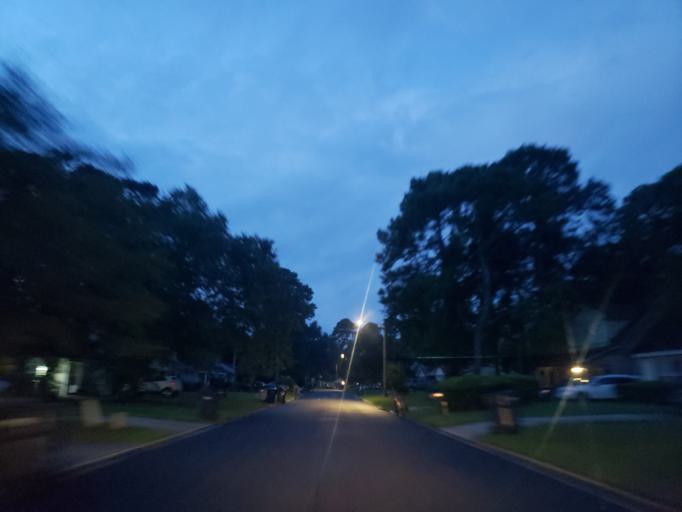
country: US
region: Georgia
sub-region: Chatham County
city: Isle of Hope
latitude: 31.9923
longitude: -81.0738
